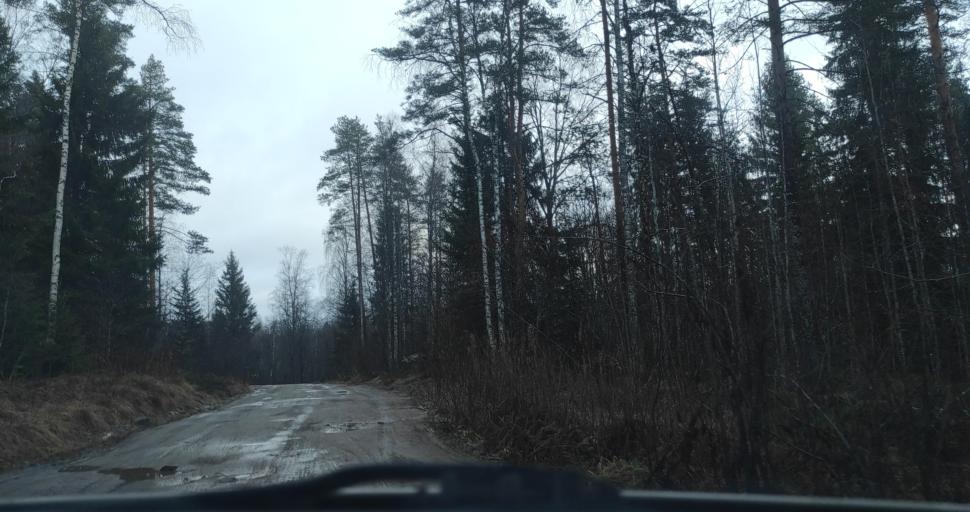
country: RU
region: Republic of Karelia
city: Pitkyaranta
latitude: 61.7454
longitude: 31.3951
